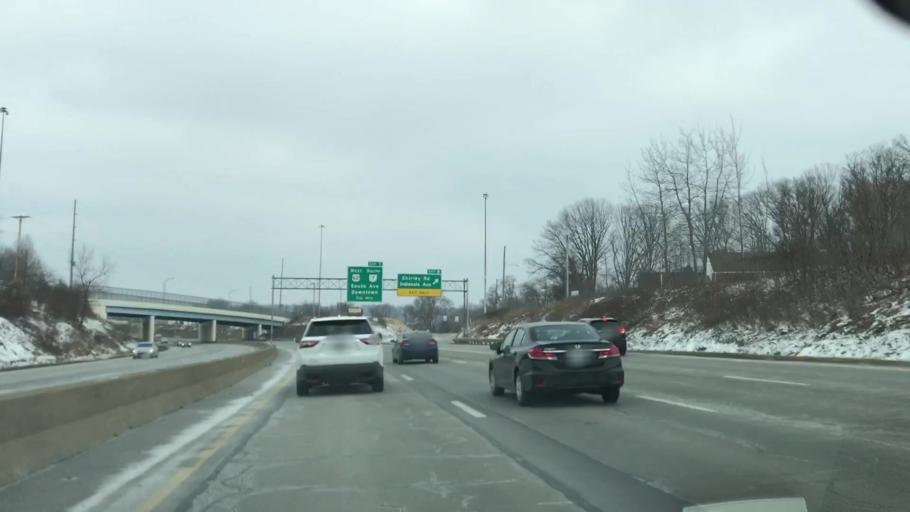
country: US
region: Ohio
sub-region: Mahoning County
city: Struthers
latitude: 41.0712
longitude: -80.6252
